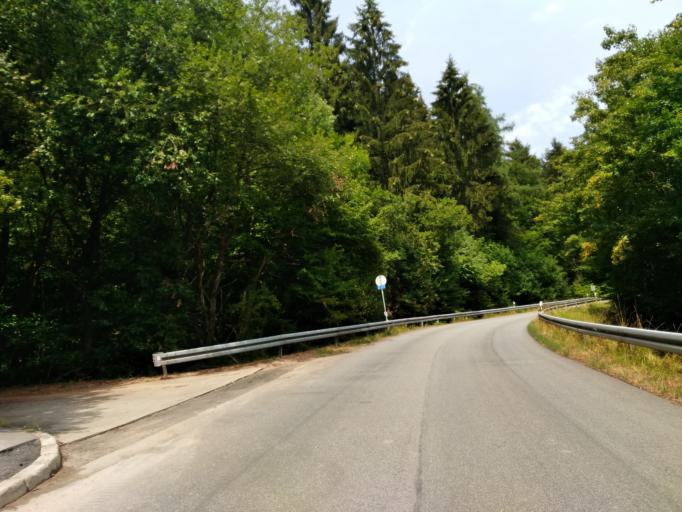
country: DE
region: Baden-Wuerttemberg
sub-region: Karlsruhe Region
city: Limbach
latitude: 49.4599
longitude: 9.1763
